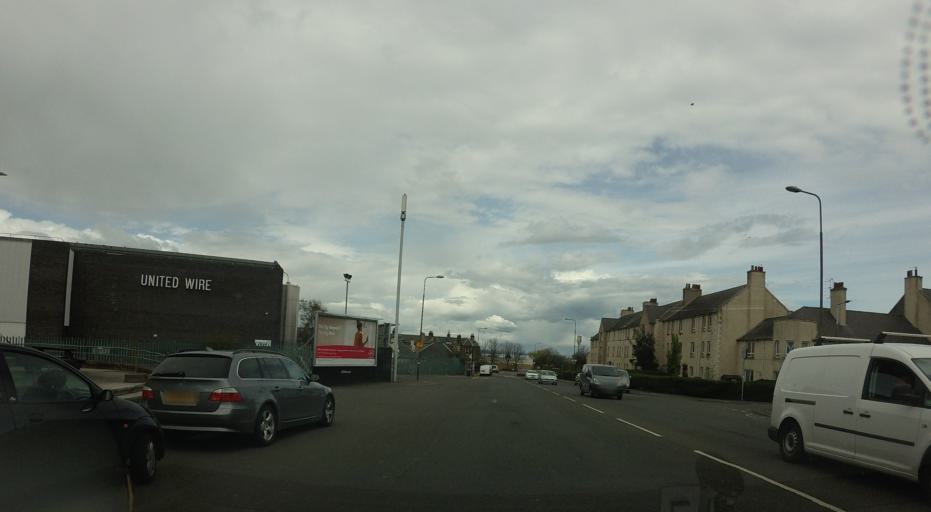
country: GB
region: Scotland
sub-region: Edinburgh
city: Edinburgh
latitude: 55.9792
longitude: -3.2312
